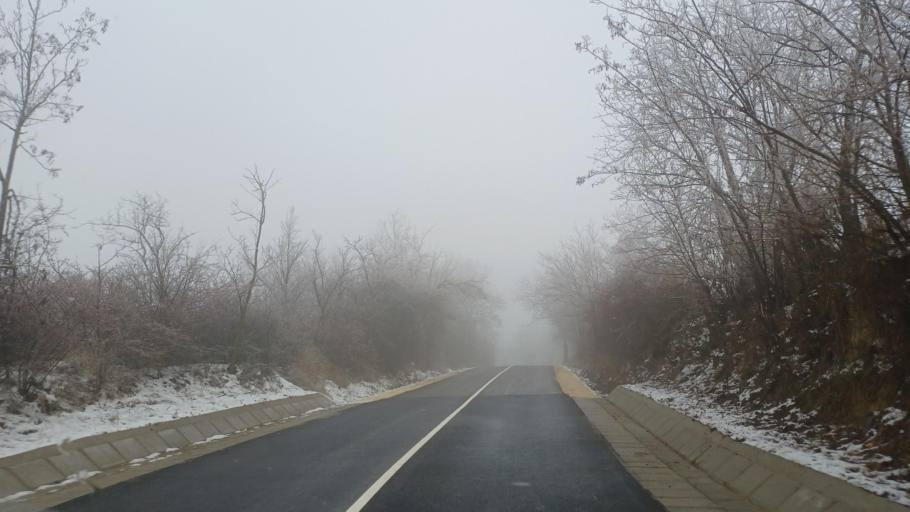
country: HU
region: Tolna
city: Gyonk
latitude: 46.5863
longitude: 18.4733
